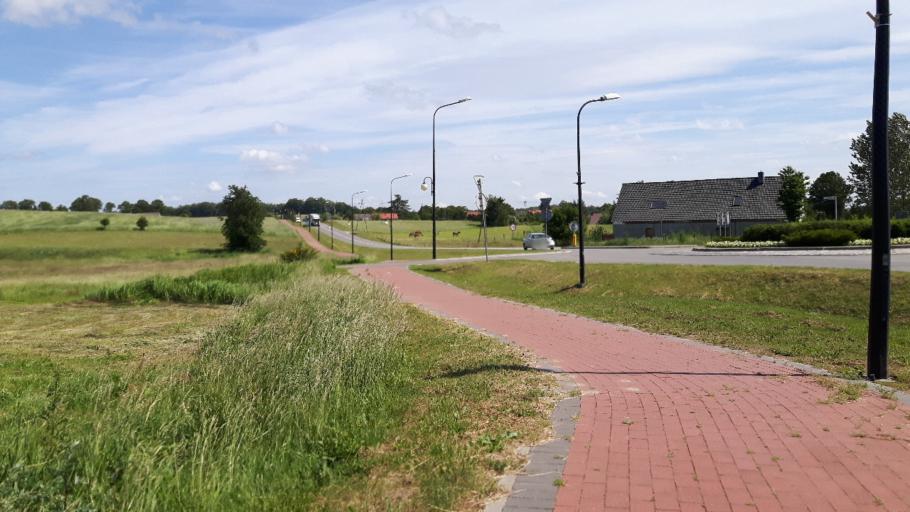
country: PL
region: Pomeranian Voivodeship
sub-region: Powiat wejherowski
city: Gniewino
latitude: 54.6876
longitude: 18.0788
